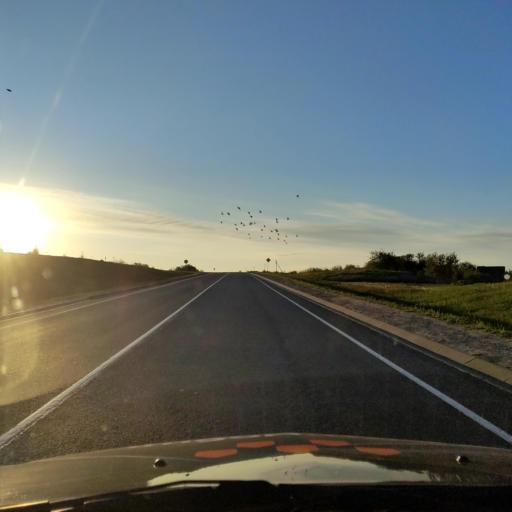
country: RU
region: Orjol
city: Livny
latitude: 52.4493
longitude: 37.6162
